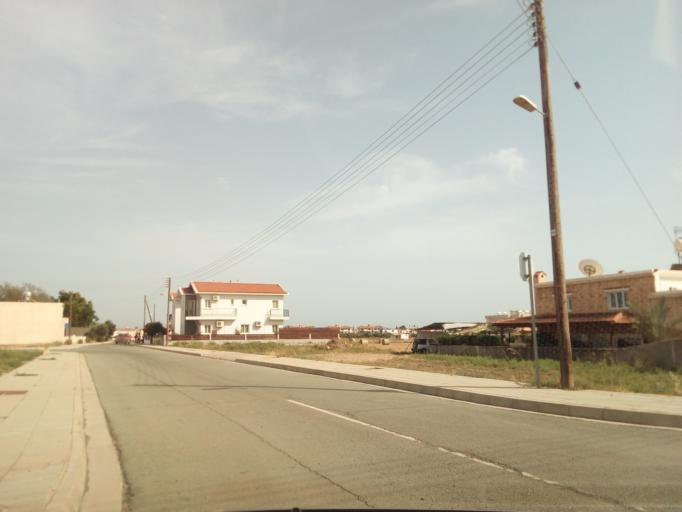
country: CY
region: Larnaka
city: Perivolia
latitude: 34.8384
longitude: 33.5770
